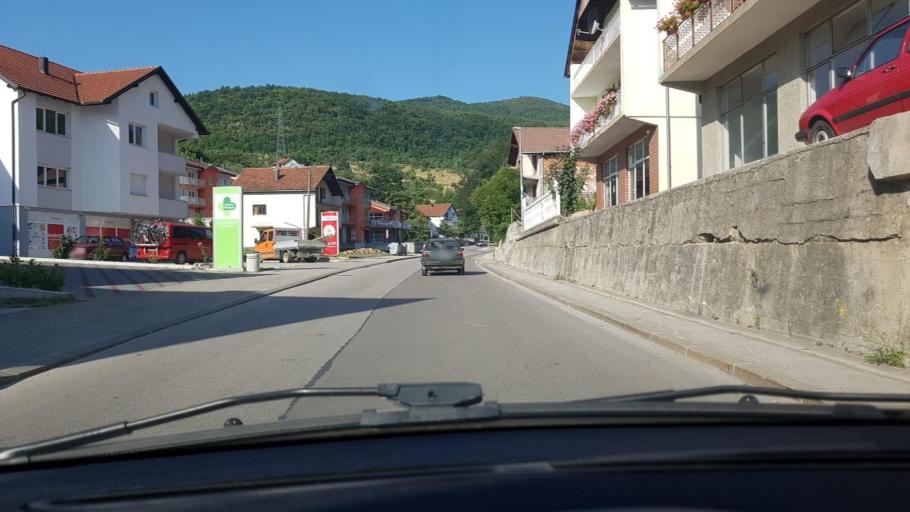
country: BA
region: Federation of Bosnia and Herzegovina
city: Prozor
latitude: 43.8230
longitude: 17.6010
